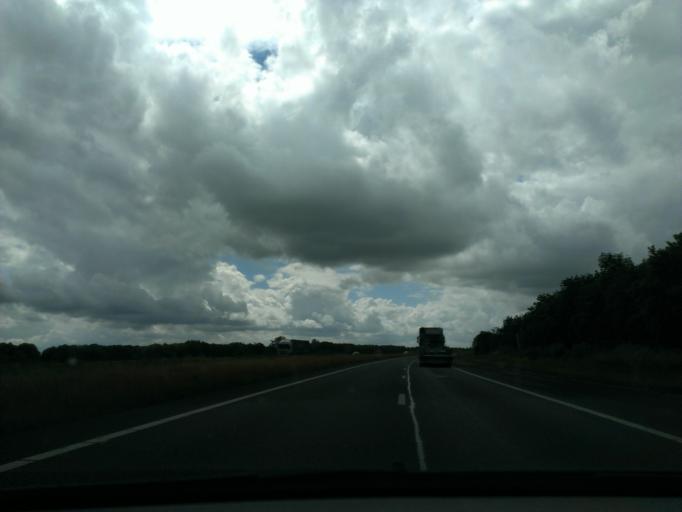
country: NL
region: Drenthe
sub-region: Gemeente Hoogeveen
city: Hoogeveen
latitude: 52.7114
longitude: 6.4975
